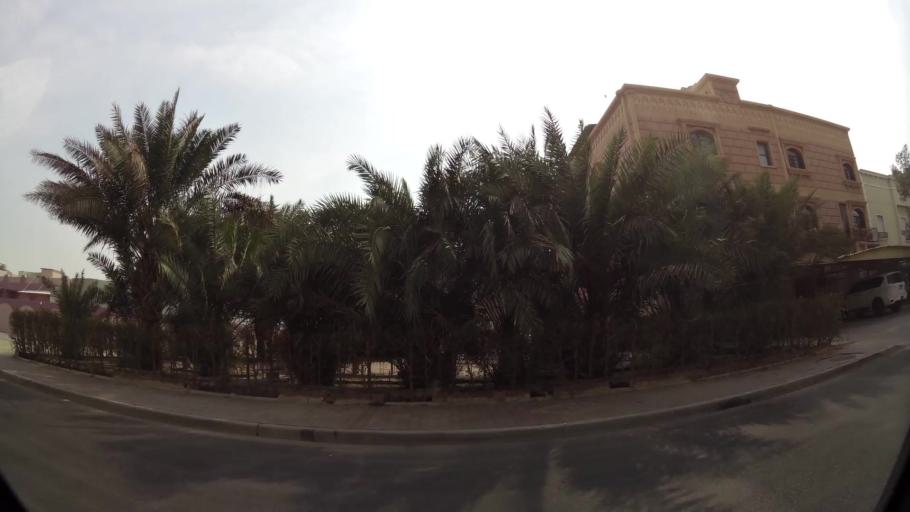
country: KW
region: Al Asimah
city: Ar Rabiyah
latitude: 29.2837
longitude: 47.9425
